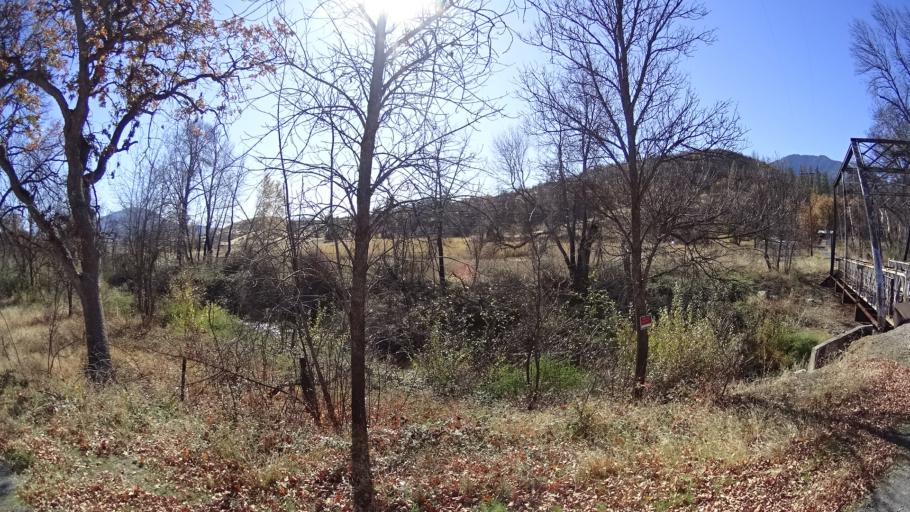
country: US
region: California
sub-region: Siskiyou County
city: Yreka
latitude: 41.9328
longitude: -122.5870
